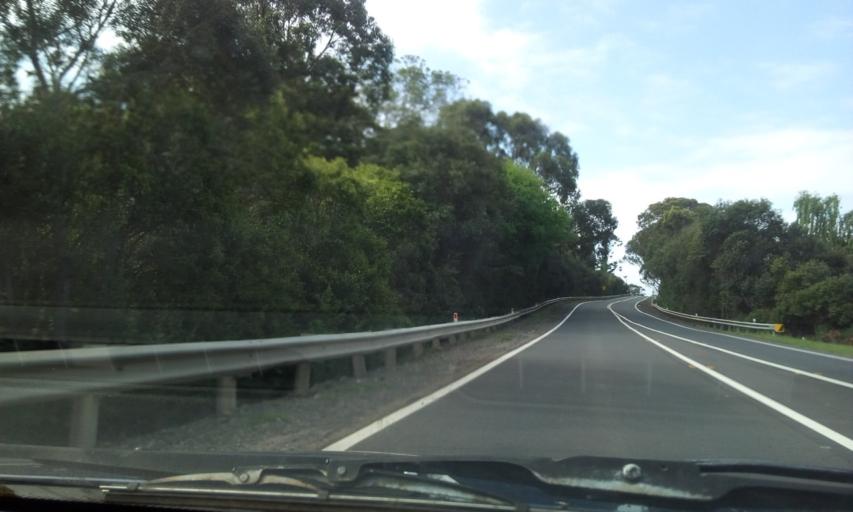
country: AU
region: New South Wales
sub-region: Campbelltown Municipality
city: Glen Alpine
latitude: -34.0926
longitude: 150.7708
